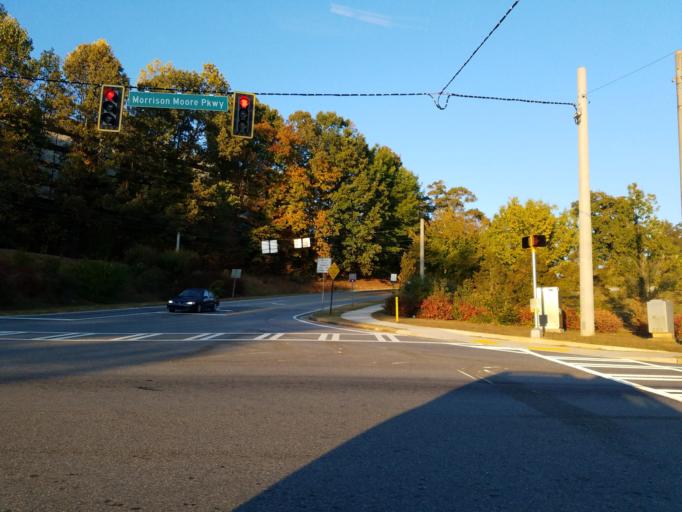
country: US
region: Georgia
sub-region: Lumpkin County
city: Dahlonega
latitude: 34.5267
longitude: -83.9907
